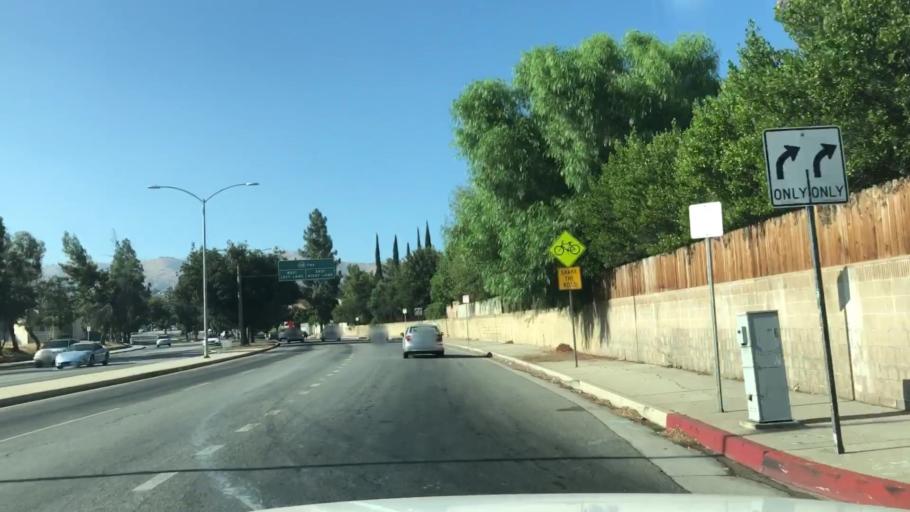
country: US
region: California
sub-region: Los Angeles County
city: Northridge
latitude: 34.2694
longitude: -118.5551
